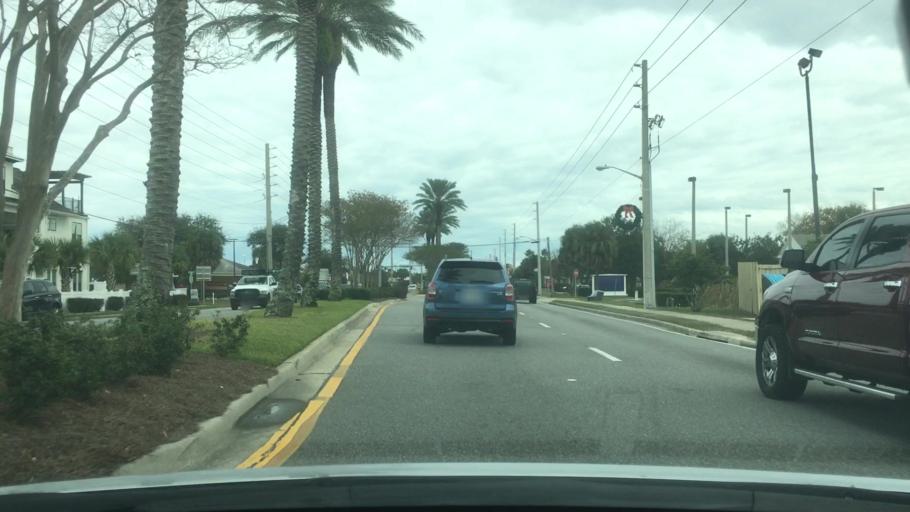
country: US
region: Florida
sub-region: Duval County
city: Atlantic Beach
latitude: 30.3246
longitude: -81.4142
